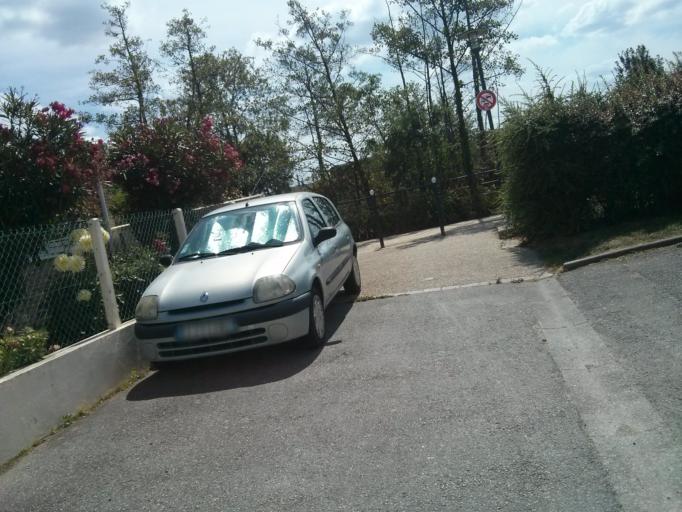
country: FR
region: Brittany
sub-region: Departement d'Ille-et-Vilaine
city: Rennes
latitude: 48.1074
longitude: -1.6540
